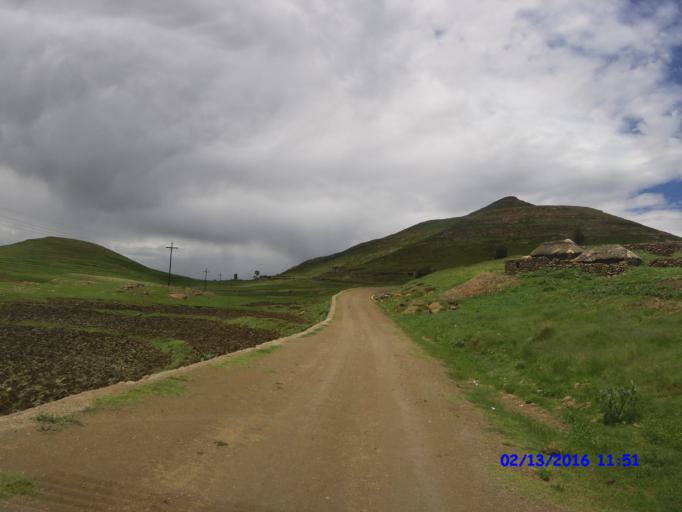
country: LS
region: Maseru
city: Nako
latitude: -29.8420
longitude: 28.0238
